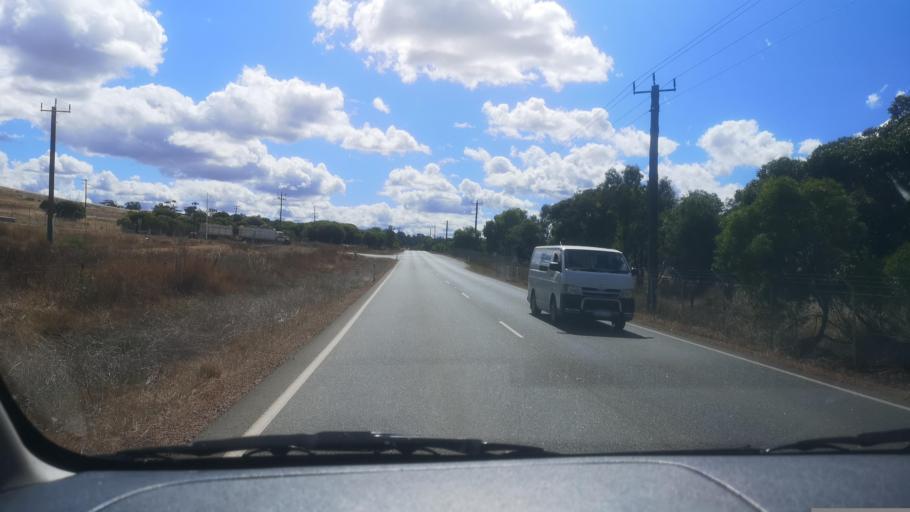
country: AU
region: Western Australia
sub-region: Northam
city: Northam
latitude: -31.6426
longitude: 116.6327
